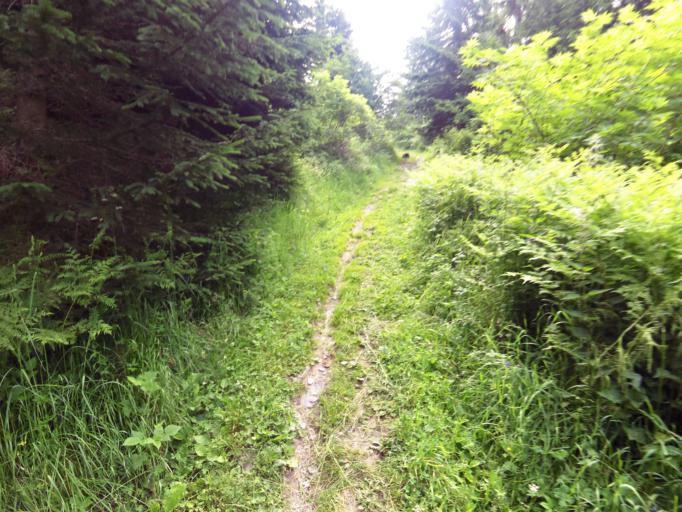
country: IT
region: Trentino-Alto Adige
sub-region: Bolzano
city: Siusi
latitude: 46.5422
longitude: 11.5901
